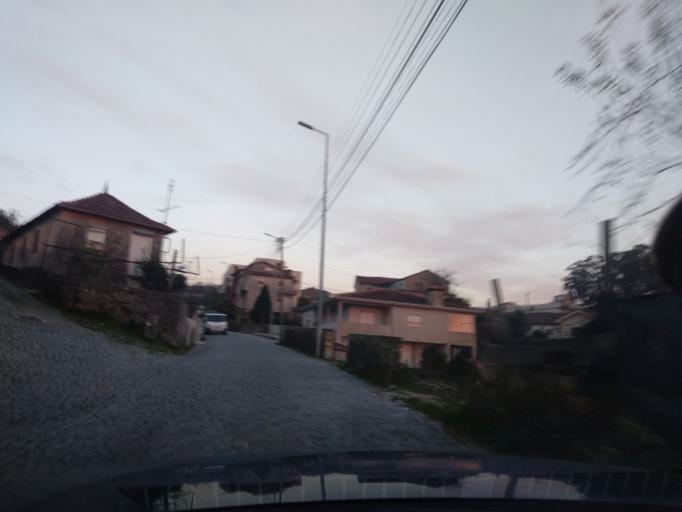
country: PT
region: Porto
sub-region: Paredes
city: Lordelo
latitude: 41.2345
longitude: -8.4044
